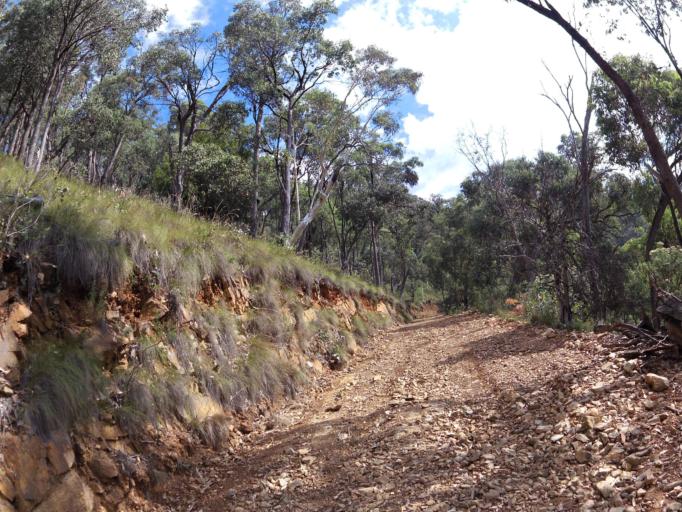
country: AU
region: Victoria
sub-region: Alpine
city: Mount Beauty
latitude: -36.7773
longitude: 147.0138
